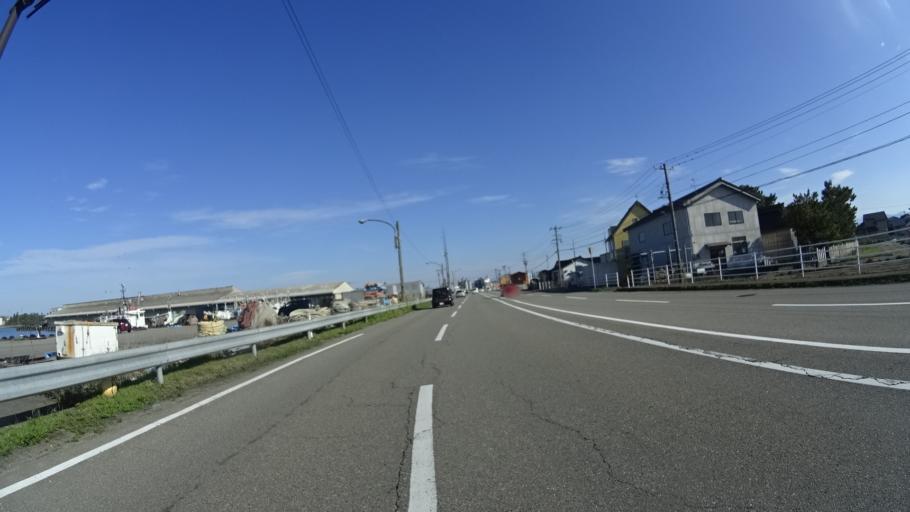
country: JP
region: Ishikawa
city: Kanazawa-shi
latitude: 36.6098
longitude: 136.6074
